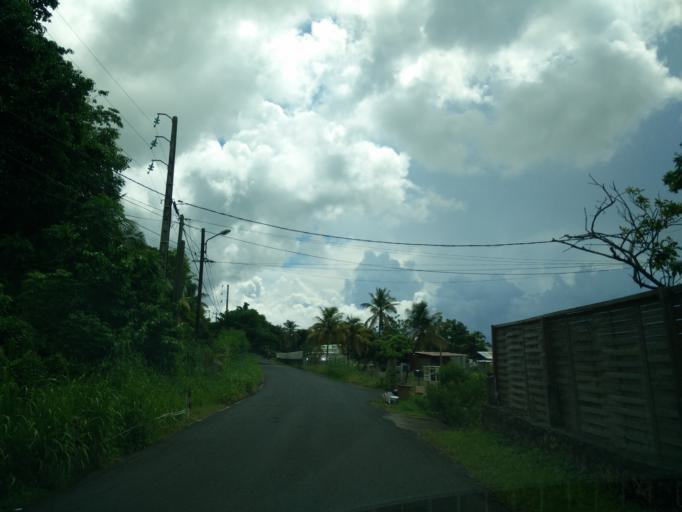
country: GP
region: Guadeloupe
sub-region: Guadeloupe
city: Saint-Francois
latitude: 16.2718
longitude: -61.3326
